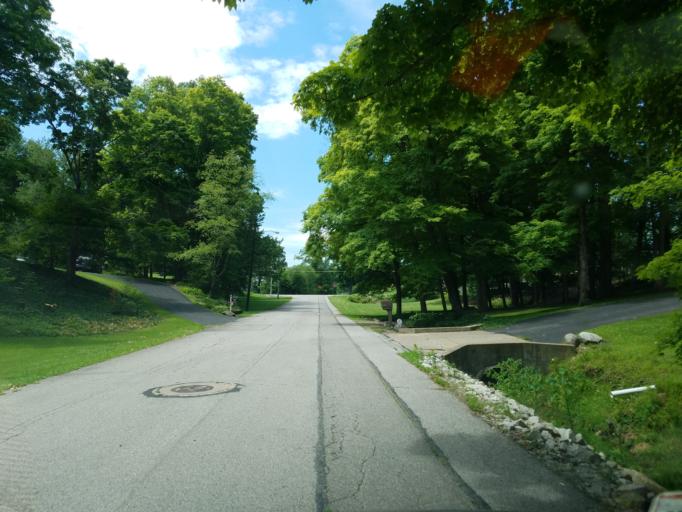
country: US
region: Ohio
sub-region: Ashland County
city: Ashland
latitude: 40.8738
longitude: -82.3332
